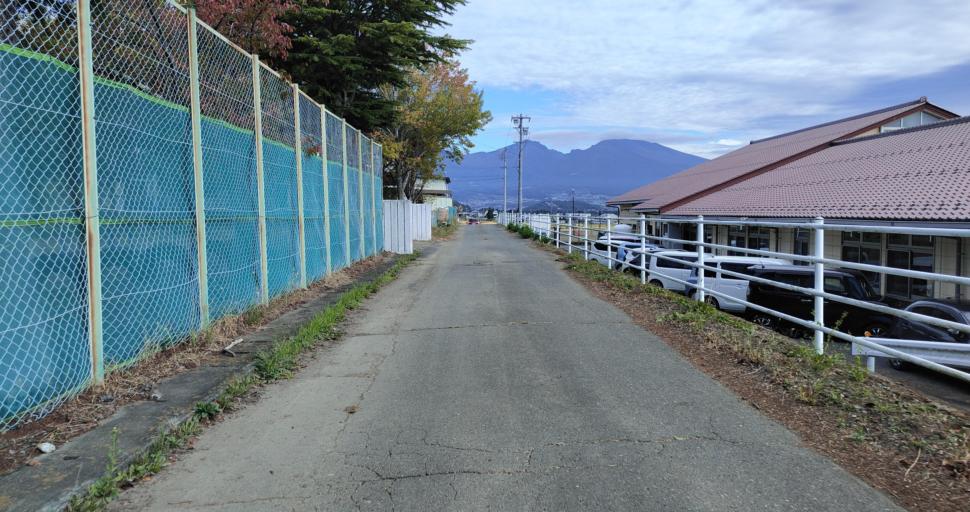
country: JP
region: Nagano
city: Komoro
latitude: 36.2678
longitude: 138.4072
